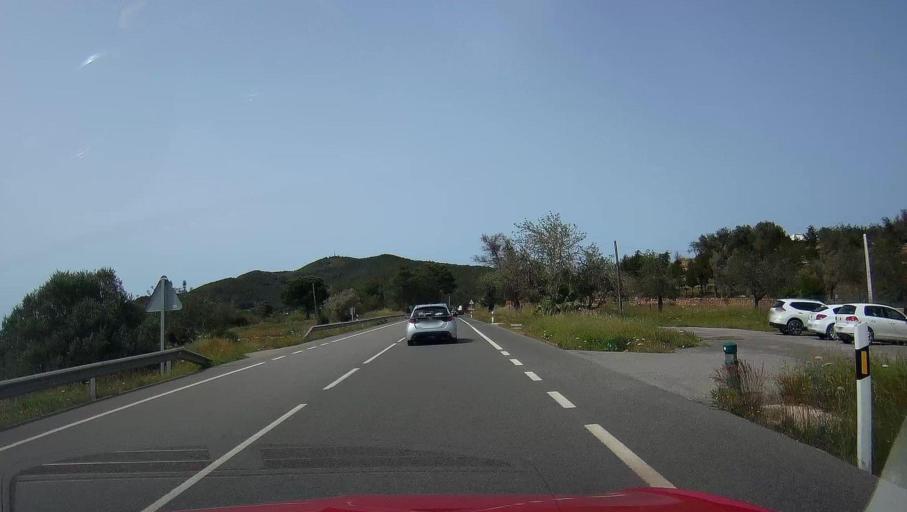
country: ES
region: Balearic Islands
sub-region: Illes Balears
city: Sant Joan de Labritja
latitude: 39.0634
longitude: 1.4947
